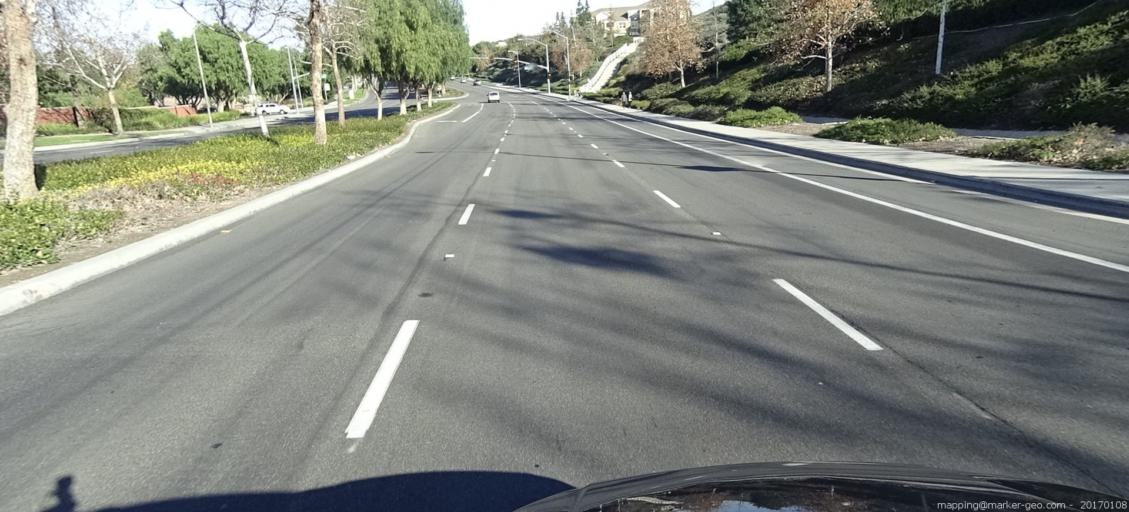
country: US
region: California
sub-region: Orange County
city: Ladera Ranch
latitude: 33.5504
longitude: -117.6294
